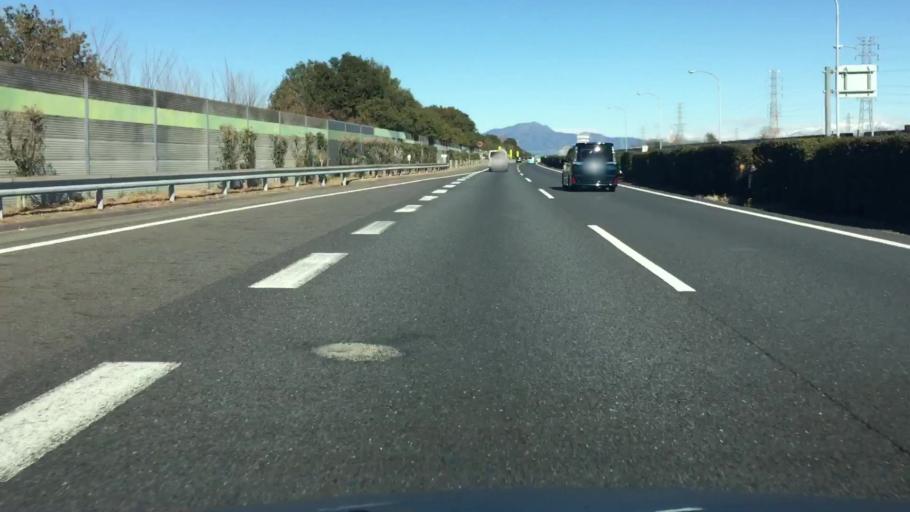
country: JP
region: Gunma
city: Maebashi-shi
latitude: 36.3761
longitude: 139.0275
